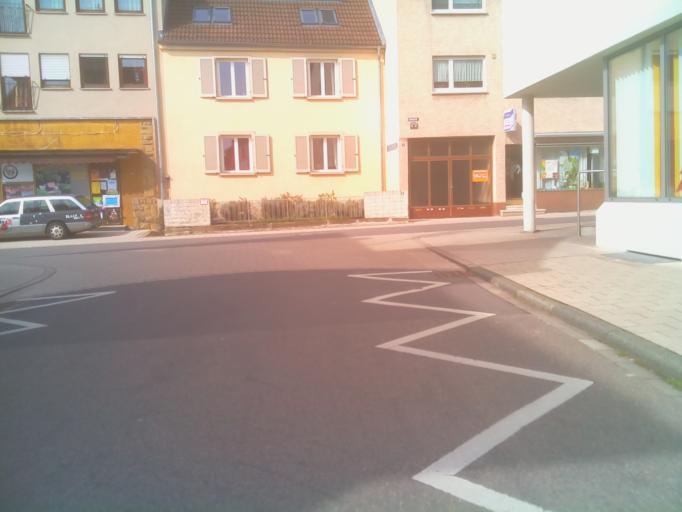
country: DE
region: Baden-Wuerttemberg
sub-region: Karlsruhe Region
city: Dossenheim
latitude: 49.4507
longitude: 8.6731
